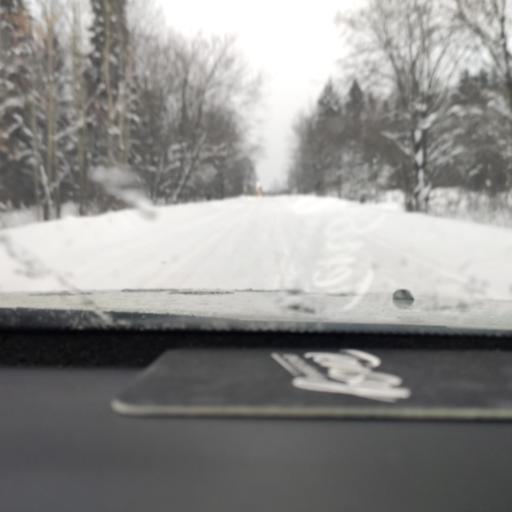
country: RU
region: Perm
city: Ferma
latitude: 57.9909
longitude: 56.3714
